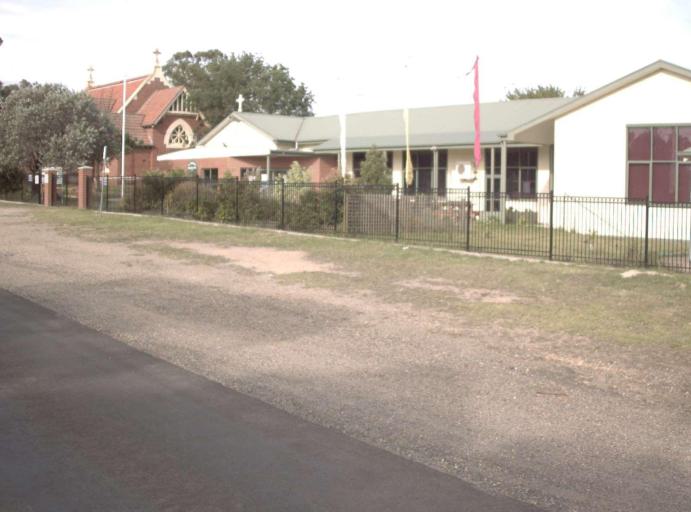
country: AU
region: Victoria
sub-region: Wellington
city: Heyfield
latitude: -37.9812
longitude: 146.7837
